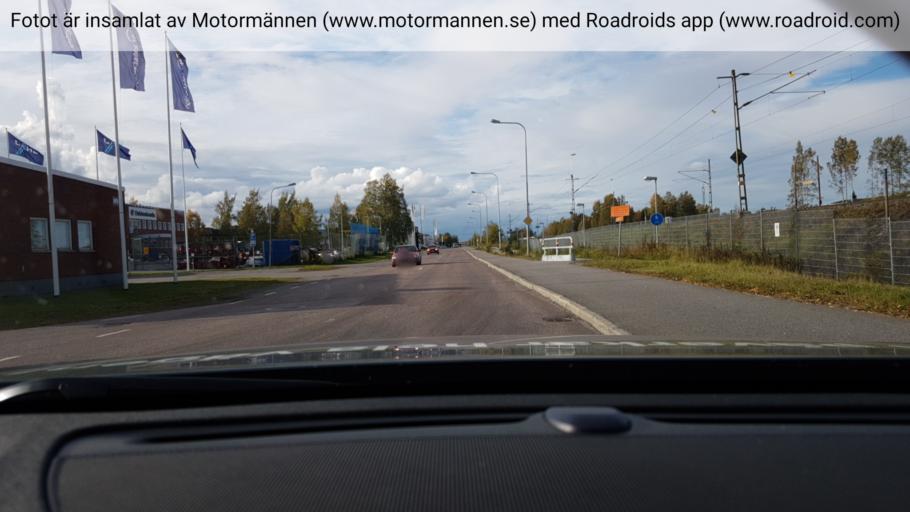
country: SE
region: Norrbotten
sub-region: Lulea Kommun
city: Bergnaset
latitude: 65.6082
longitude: 22.1259
